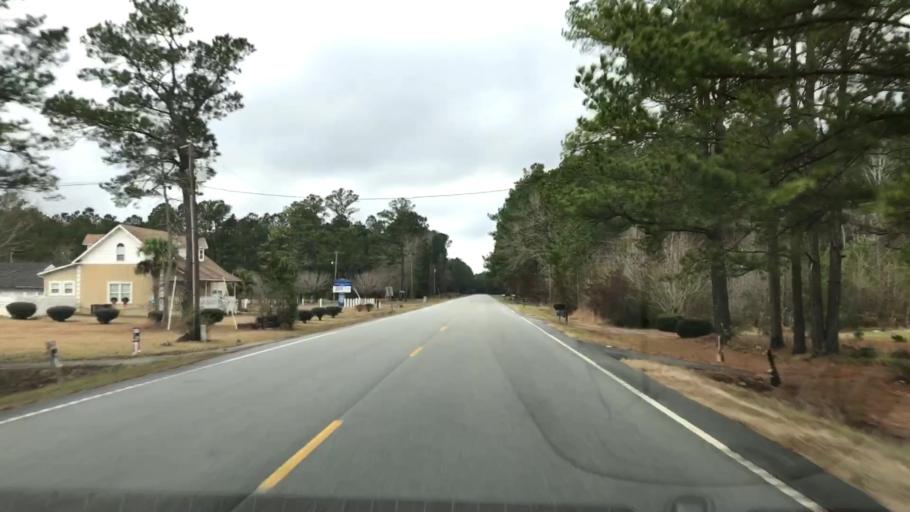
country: US
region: South Carolina
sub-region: Berkeley County
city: Saint Stephen
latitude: 33.2884
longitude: -79.7643
